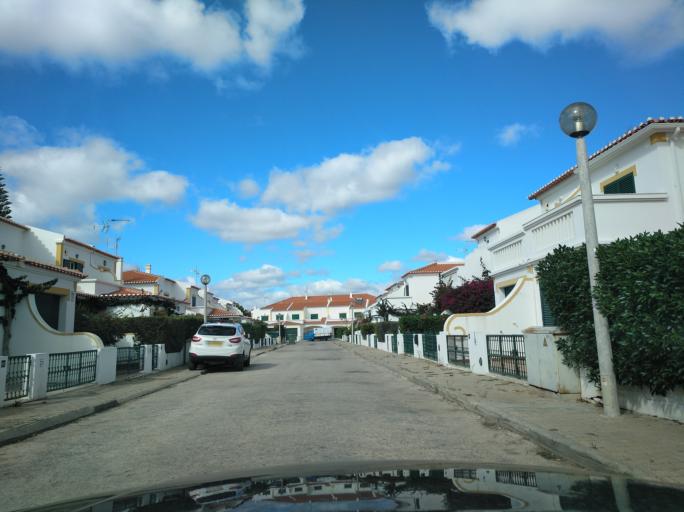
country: PT
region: Faro
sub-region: Vila Real de Santo Antonio
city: Monte Gordo
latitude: 37.1717
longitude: -7.5052
